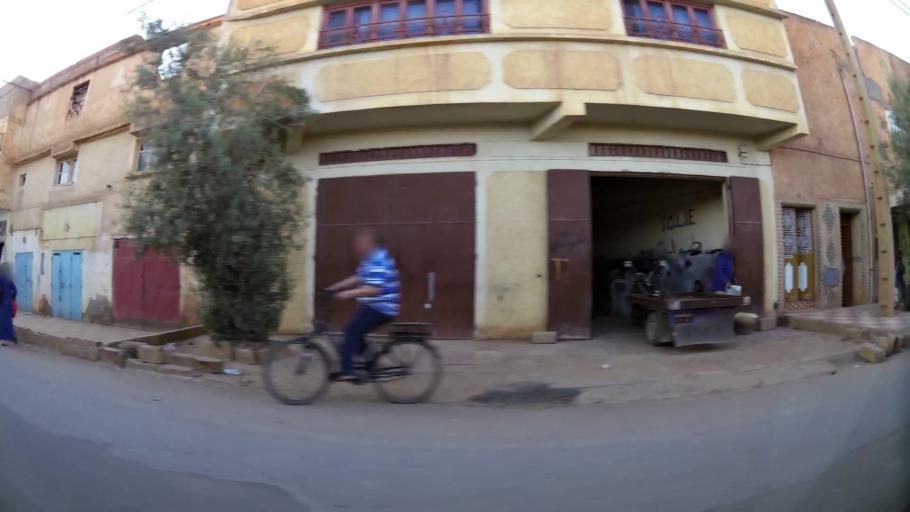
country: MA
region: Oriental
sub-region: Berkane-Taourirt
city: Berkane
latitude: 34.9216
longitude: -2.3135
